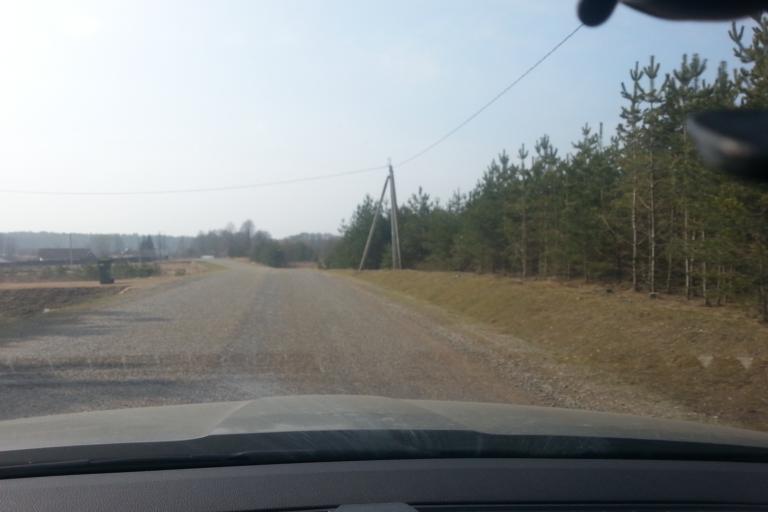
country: LT
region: Vilnius County
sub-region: Trakai
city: Rudiskes
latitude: 54.5195
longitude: 24.9424
